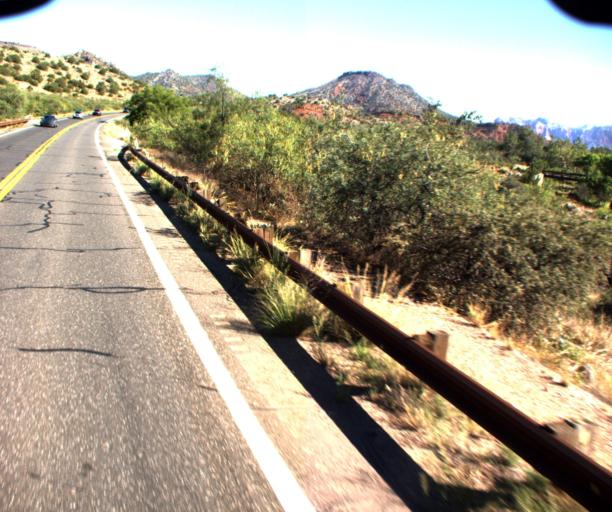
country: US
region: Arizona
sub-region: Yavapai County
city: Big Park
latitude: 34.7275
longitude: -111.7764
